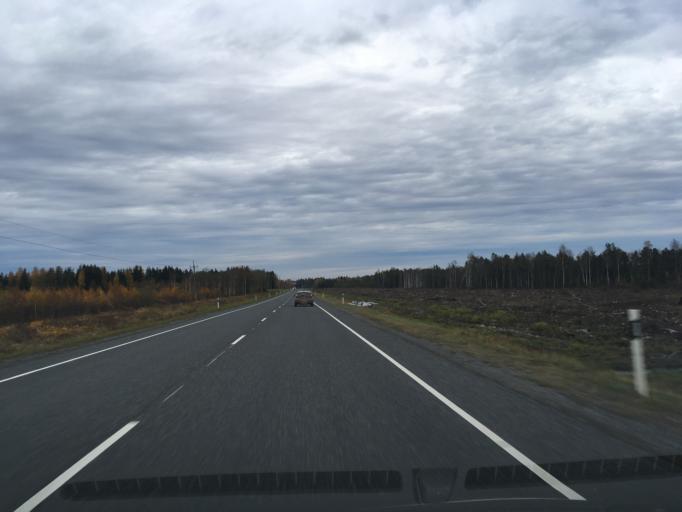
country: EE
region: Harju
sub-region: Nissi vald
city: Turba
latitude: 58.9844
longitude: 24.0578
